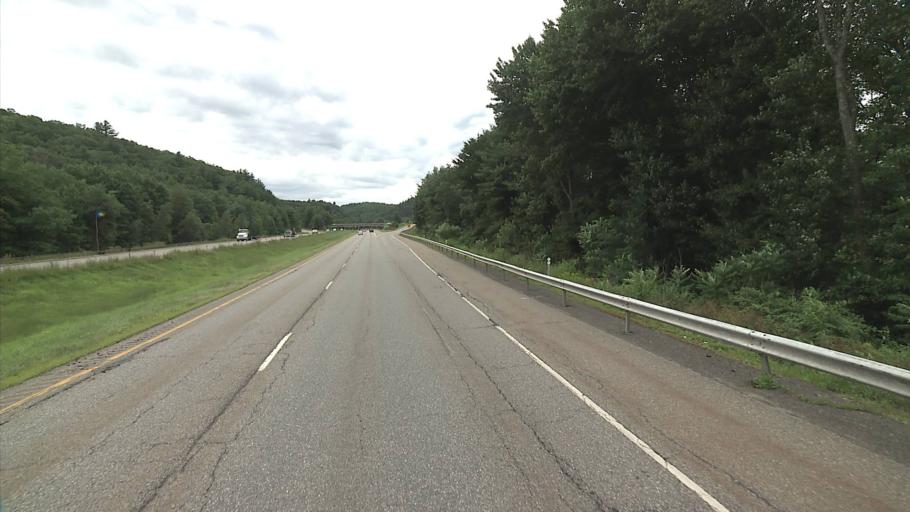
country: US
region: Connecticut
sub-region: Litchfield County
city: Torrington
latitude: 41.7672
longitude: -73.1153
